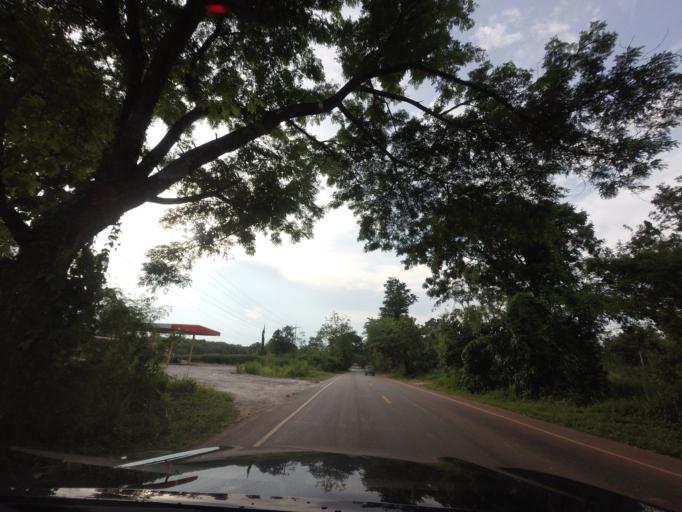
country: TH
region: Nong Khai
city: Pho Tak
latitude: 17.7846
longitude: 102.3725
